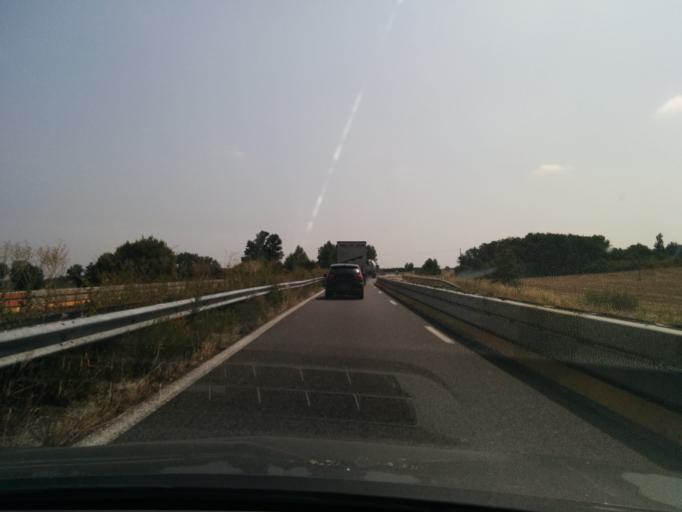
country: FR
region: Midi-Pyrenees
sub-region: Departement du Tarn
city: Saint-Sulpice-la-Pointe
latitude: 43.7551
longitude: 1.6655
